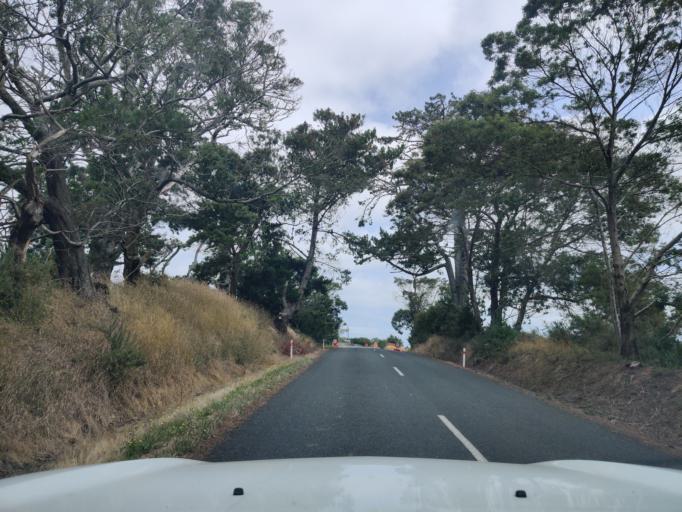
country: NZ
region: Waikato
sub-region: Waikato District
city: Te Kauwhata
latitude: -37.5180
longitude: 175.1769
